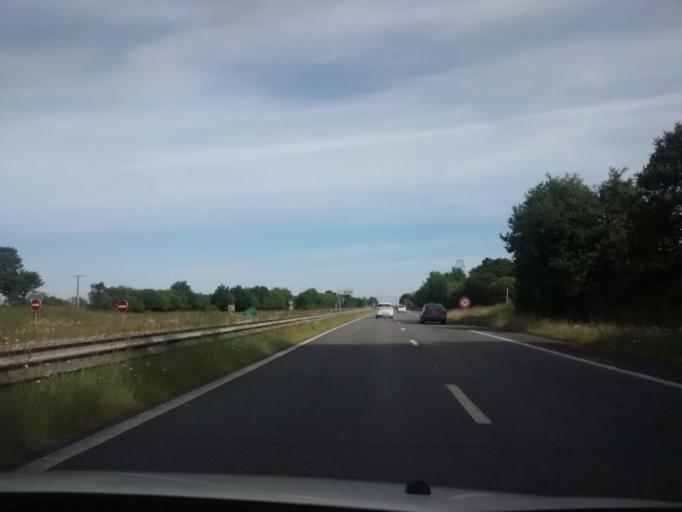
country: FR
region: Brittany
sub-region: Departement d'Ille-et-Vilaine
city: Quedillac
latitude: 48.2524
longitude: -2.1378
